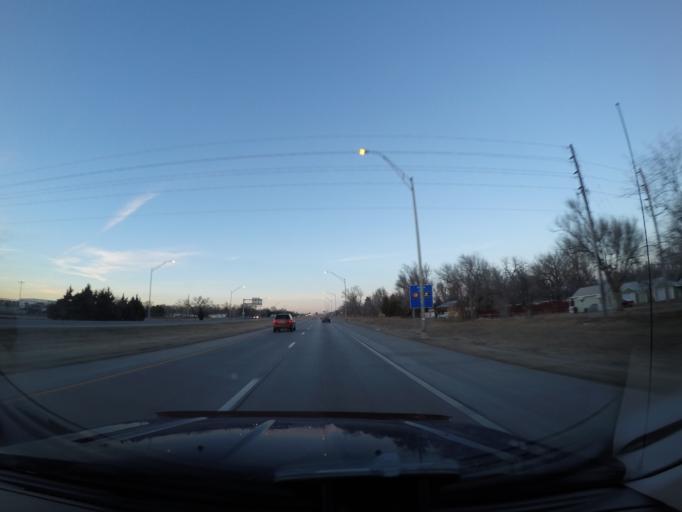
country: US
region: Kansas
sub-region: Sedgwick County
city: Wichita
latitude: 37.6871
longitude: -97.4089
